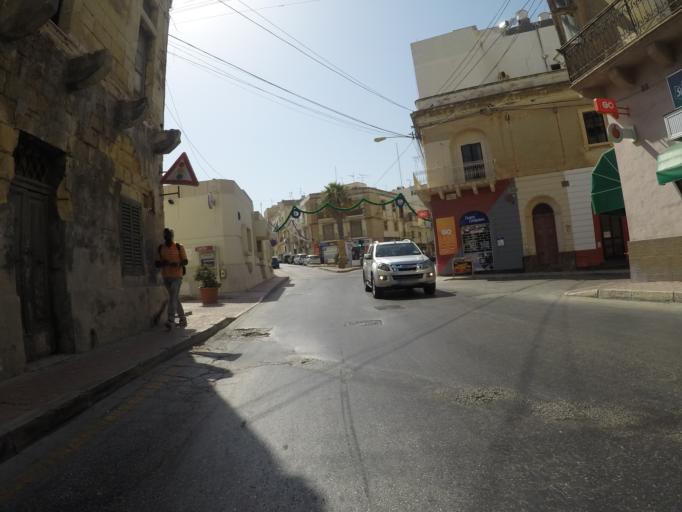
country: MT
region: Saint Paul's Bay
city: San Pawl il-Bahar
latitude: 35.9478
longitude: 14.4050
